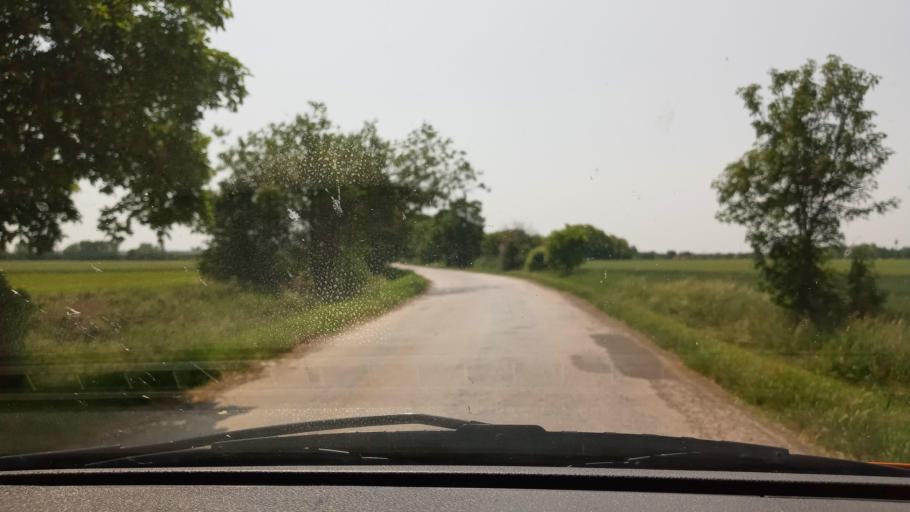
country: HU
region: Baranya
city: Szentlorinc
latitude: 46.0164
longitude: 18.0352
